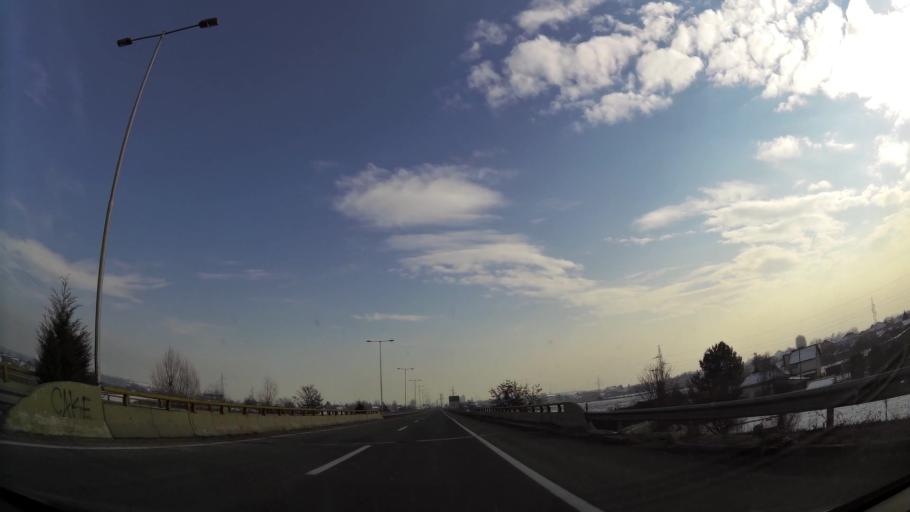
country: MK
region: Butel
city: Butel
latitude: 42.0451
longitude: 21.4423
